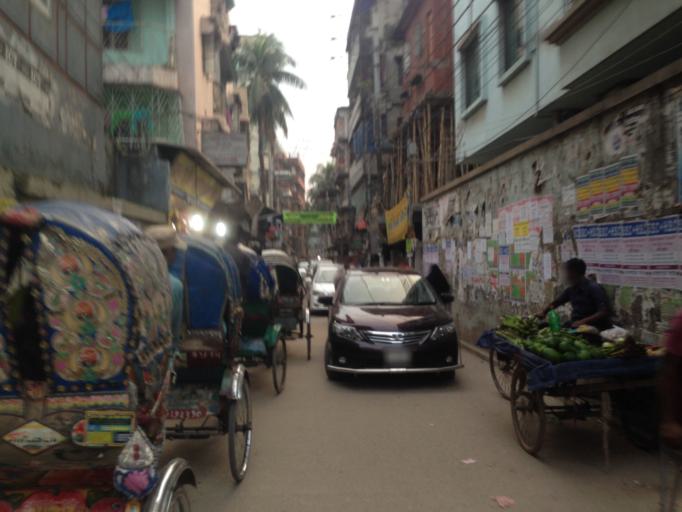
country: BD
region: Dhaka
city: Paltan
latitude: 23.7455
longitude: 90.4243
